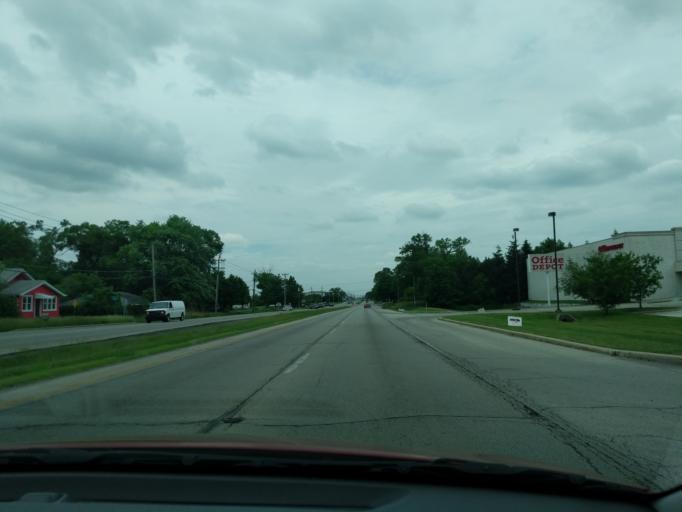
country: US
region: Indiana
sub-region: Madison County
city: Anderson
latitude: 40.0773
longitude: -85.6527
